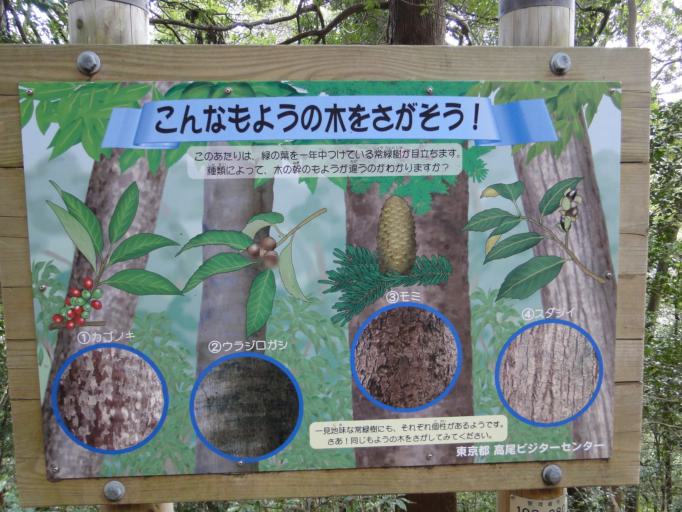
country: JP
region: Tokyo
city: Hachioji
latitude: 35.6241
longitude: 139.2510
